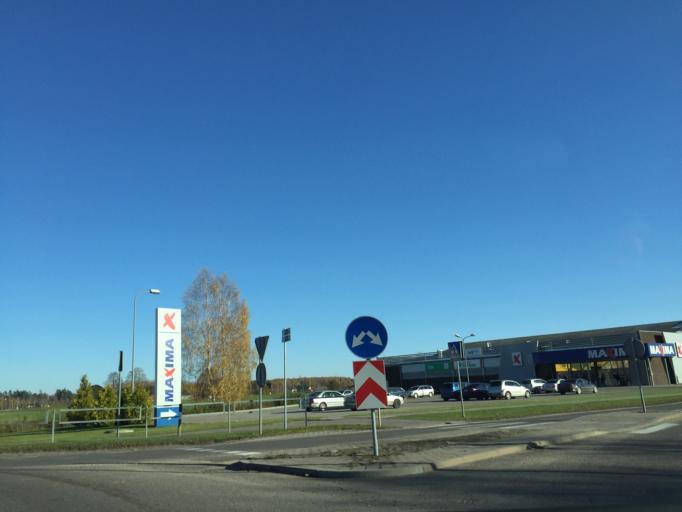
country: LV
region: Aizkraukles Rajons
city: Aizkraukle
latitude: 56.6086
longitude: 25.2580
